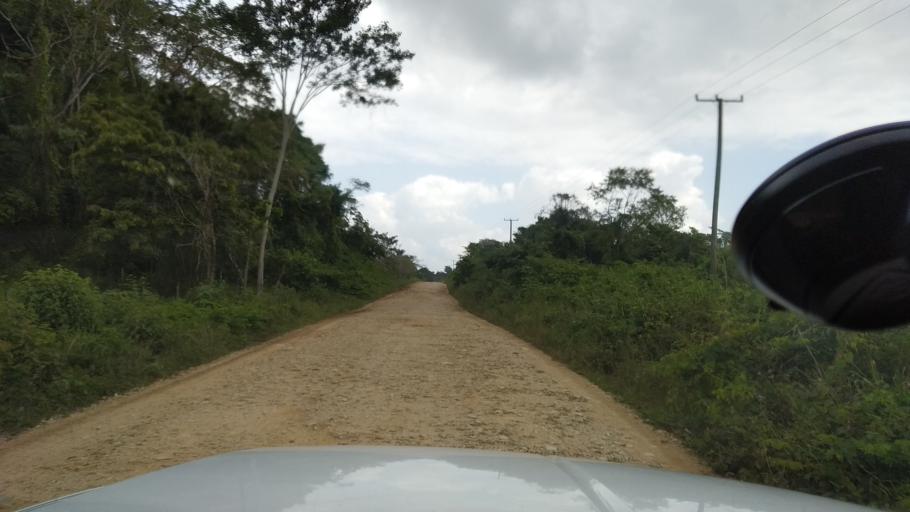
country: BZ
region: Toledo
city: Punta Gorda
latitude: 16.2171
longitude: -89.0044
